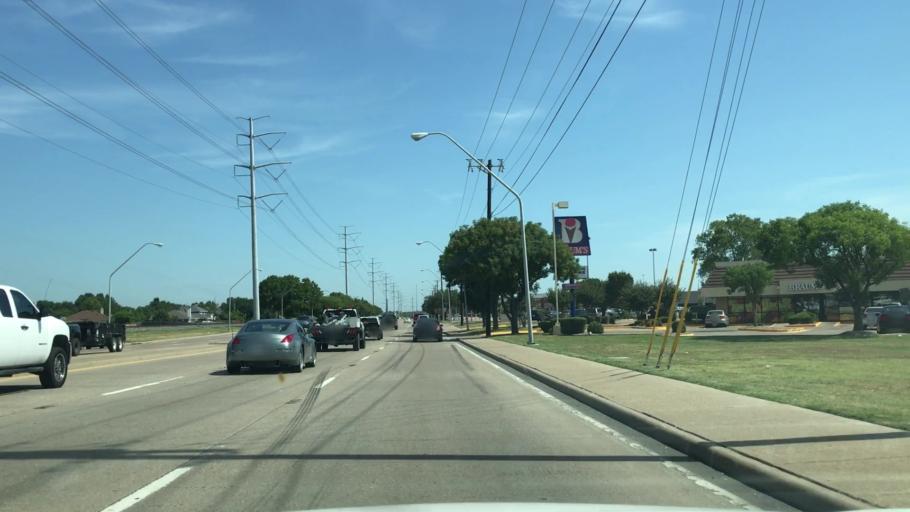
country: US
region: Texas
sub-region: Dallas County
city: Garland
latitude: 32.9408
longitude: -96.6224
